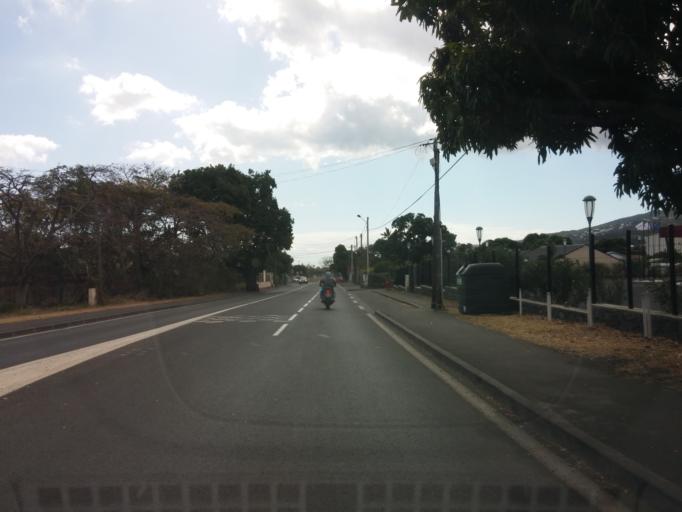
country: RE
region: Reunion
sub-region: Reunion
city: La Possession
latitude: -20.9474
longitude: 55.3272
